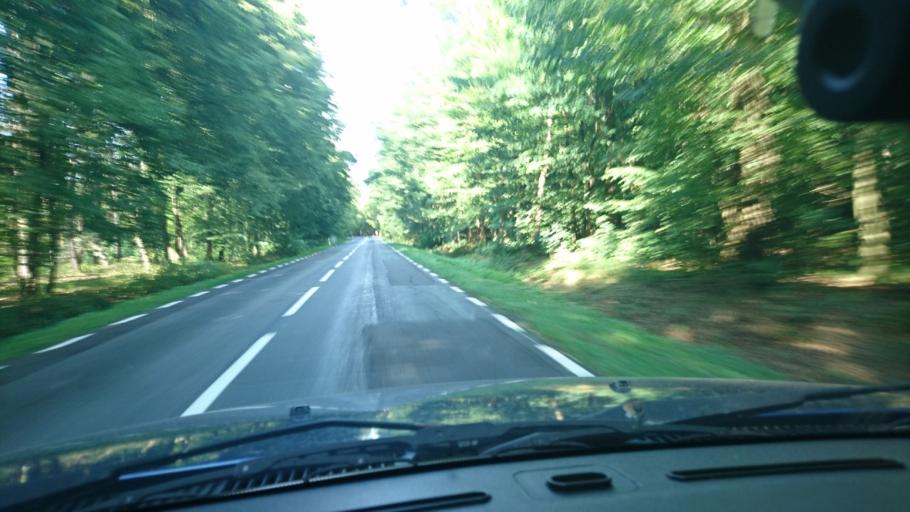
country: PL
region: Greater Poland Voivodeship
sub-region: Powiat krotoszynski
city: Krotoszyn
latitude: 51.6522
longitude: 17.4798
